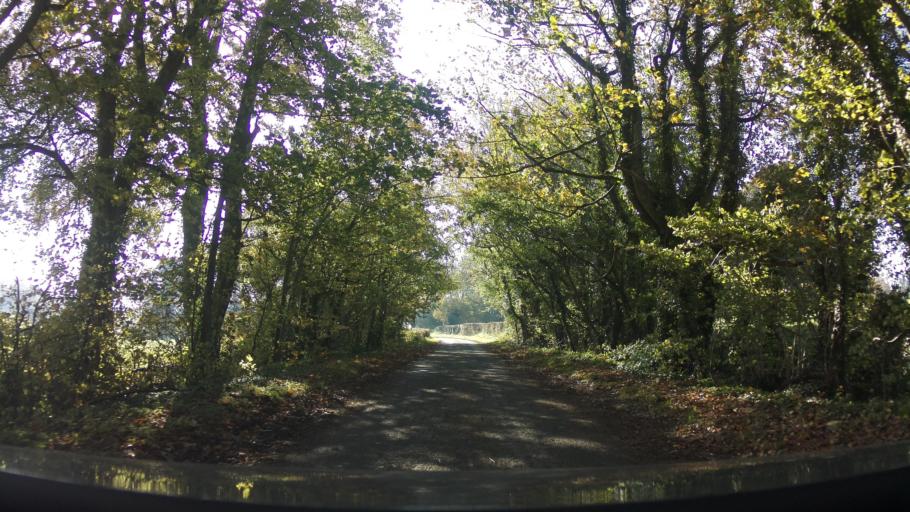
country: GB
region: England
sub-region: Somerset
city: Castle Cary
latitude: 51.0558
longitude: -2.4826
